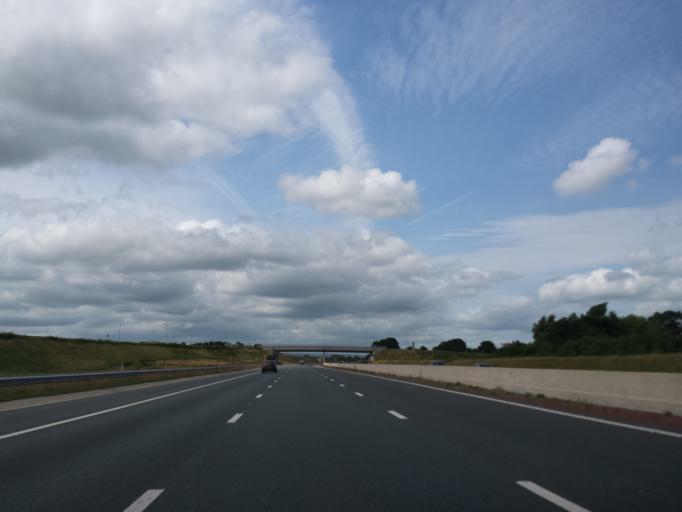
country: GB
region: England
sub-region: North Yorkshire
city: Bedale
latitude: 54.2812
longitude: -1.5373
